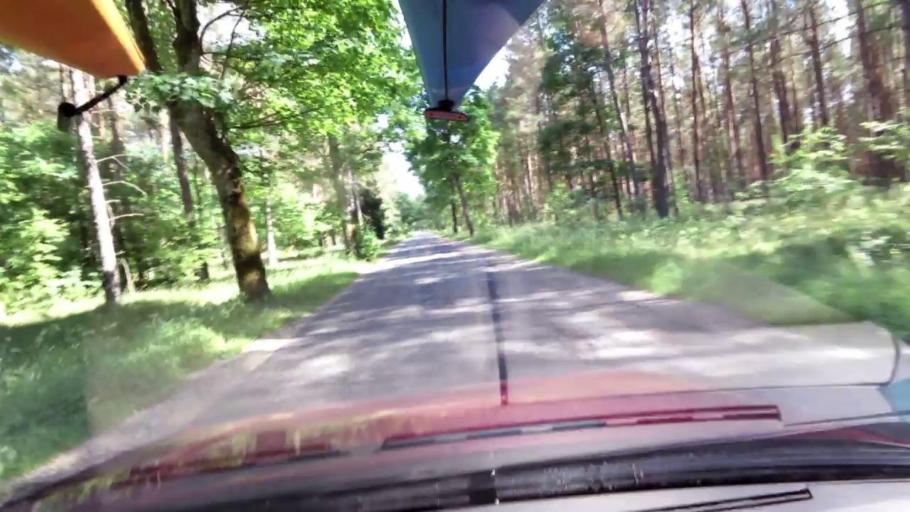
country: PL
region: Pomeranian Voivodeship
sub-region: Powiat slupski
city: Kepice
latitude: 54.1407
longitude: 16.9218
